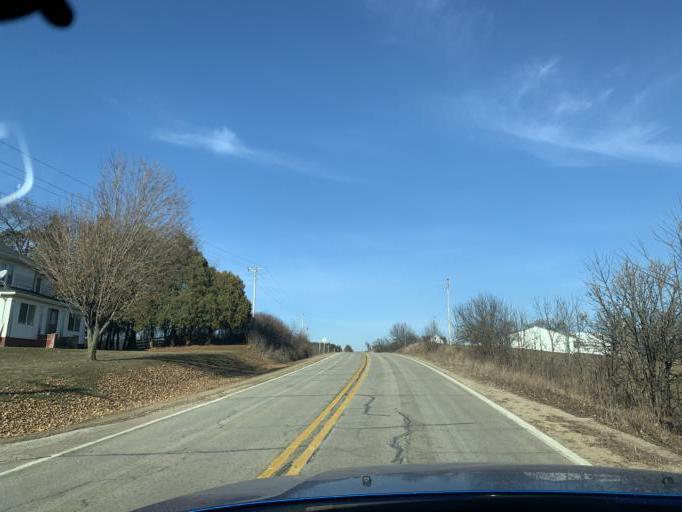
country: US
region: Wisconsin
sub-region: Green County
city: New Glarus
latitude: 42.7649
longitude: -89.8583
